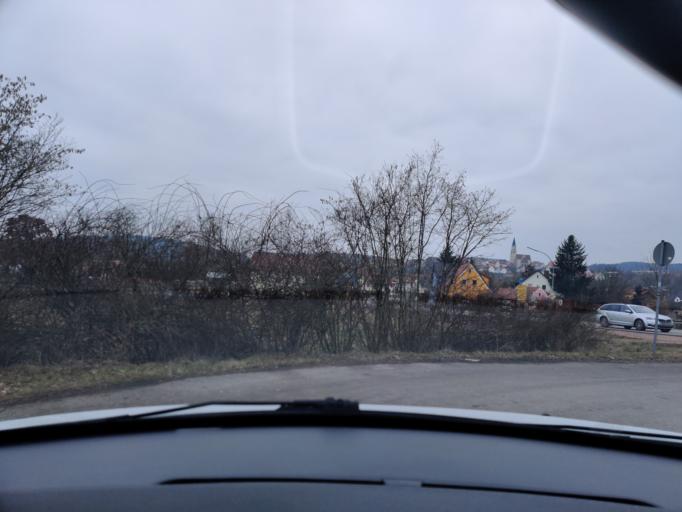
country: DE
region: Bavaria
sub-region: Upper Palatinate
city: Nabburg
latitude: 49.4549
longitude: 12.1920
